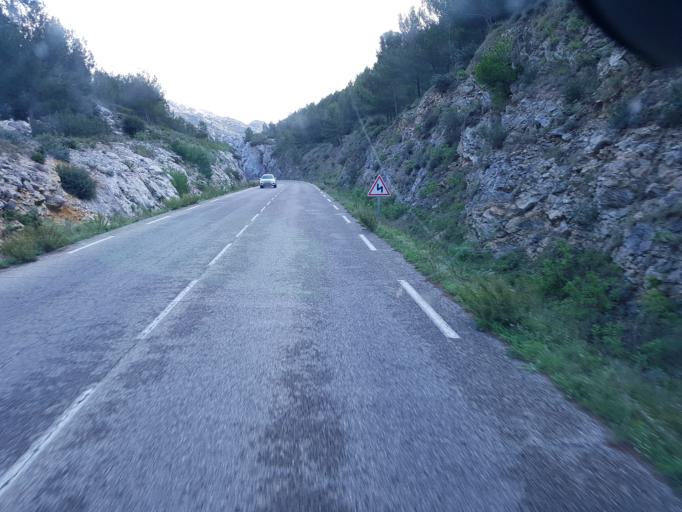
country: FR
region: Provence-Alpes-Cote d'Azur
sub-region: Departement des Bouches-du-Rhone
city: Le Rove
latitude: 43.3503
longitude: 5.2403
